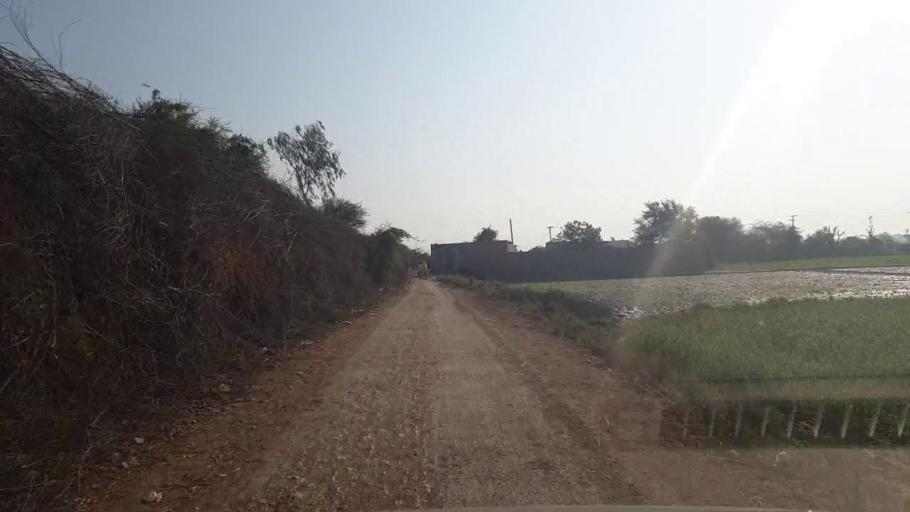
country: PK
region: Sindh
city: Tando Adam
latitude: 25.7470
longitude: 68.6050
